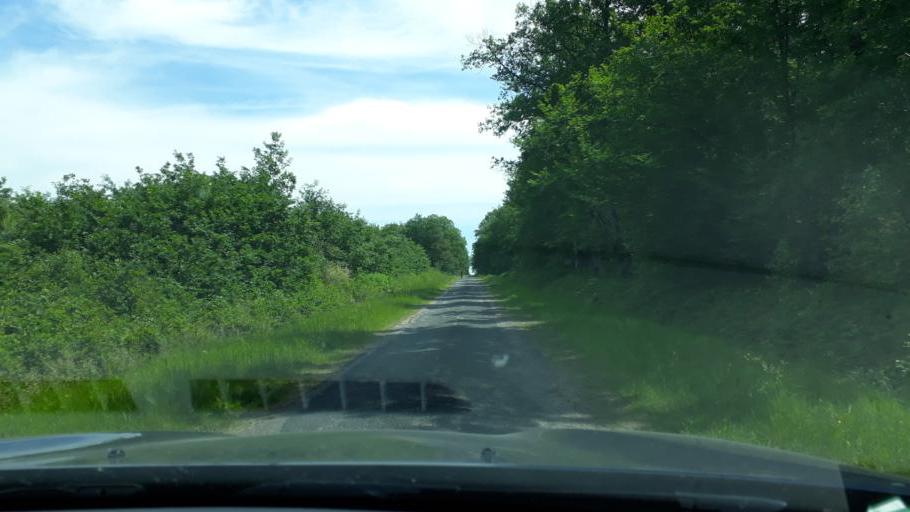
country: FR
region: Centre
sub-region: Departement du Loiret
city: Vitry-aux-Loges
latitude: 48.0235
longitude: 2.2704
